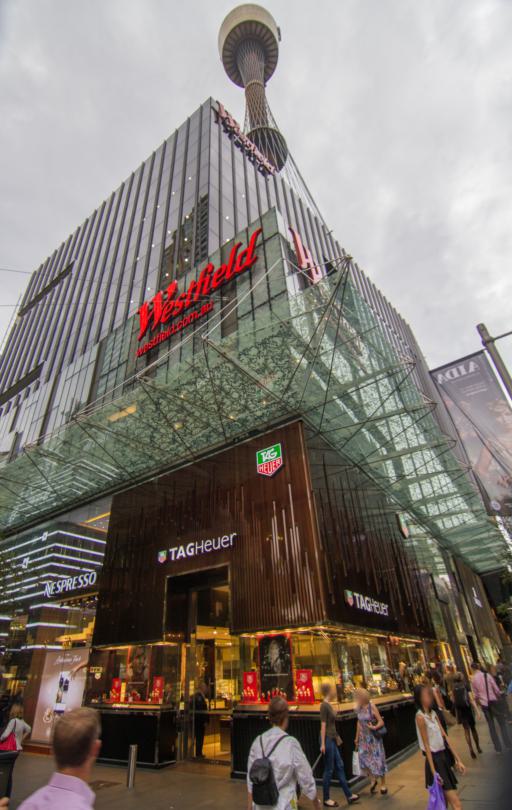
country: AU
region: New South Wales
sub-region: City of Sydney
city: Sydney
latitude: -33.8706
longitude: 151.2084
